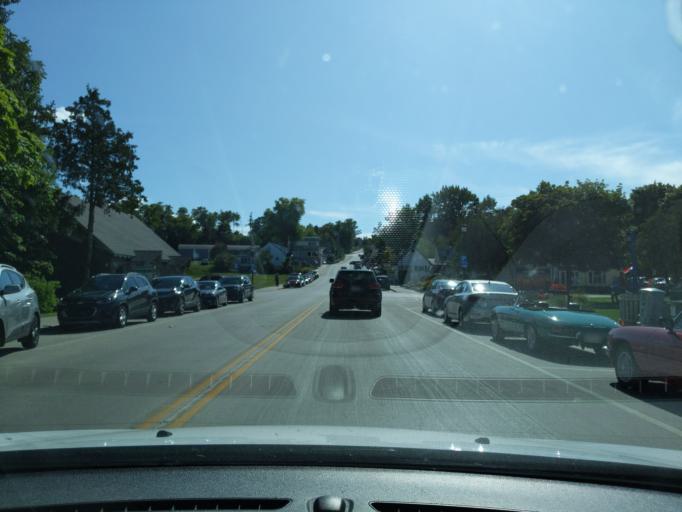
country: US
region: Wisconsin
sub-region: Door County
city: Sturgeon Bay
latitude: 45.1889
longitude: -87.1213
